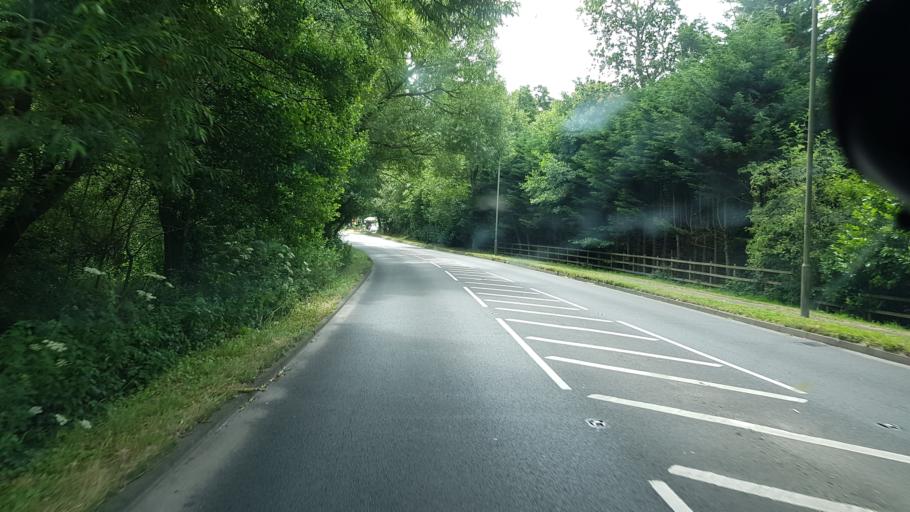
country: GB
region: England
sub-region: Surrey
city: Felbridge
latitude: 51.1551
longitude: -0.0500
